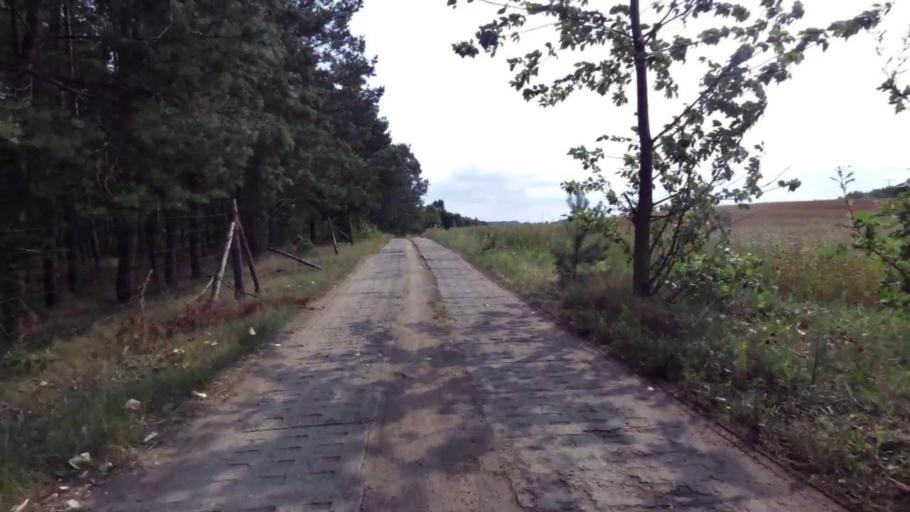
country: PL
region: West Pomeranian Voivodeship
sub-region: Powiat drawski
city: Czaplinek
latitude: 53.5730
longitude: 16.2438
